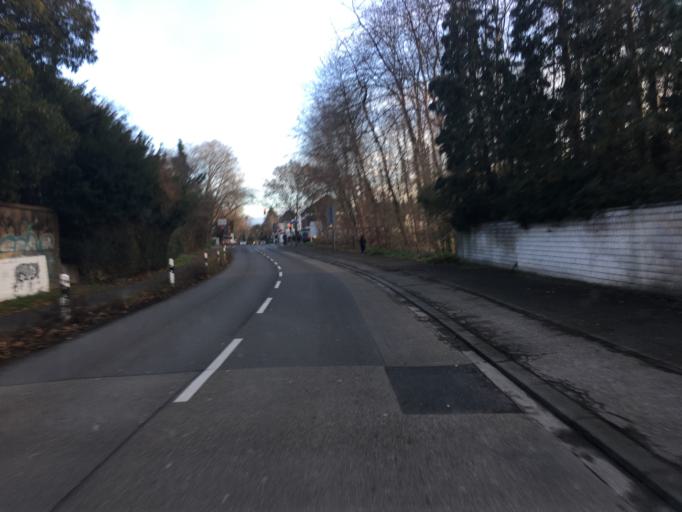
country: DE
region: North Rhine-Westphalia
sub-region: Regierungsbezirk Koln
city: Poll
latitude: 50.8815
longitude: 7.0131
